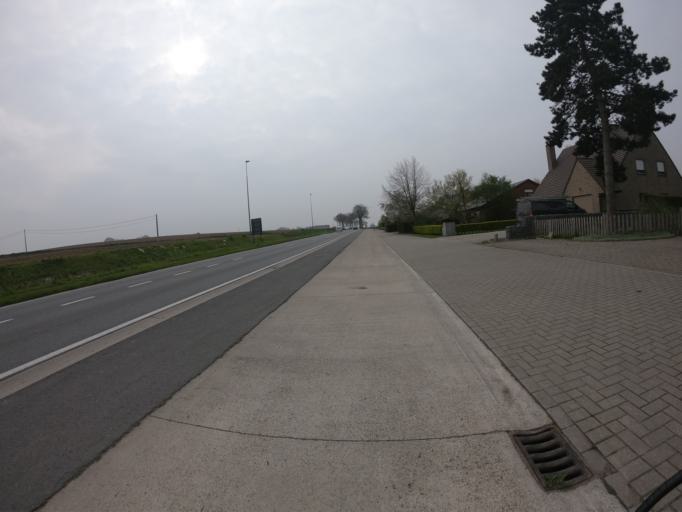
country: BE
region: Flanders
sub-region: Provincie West-Vlaanderen
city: Zwevegem
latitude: 50.7971
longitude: 3.3688
